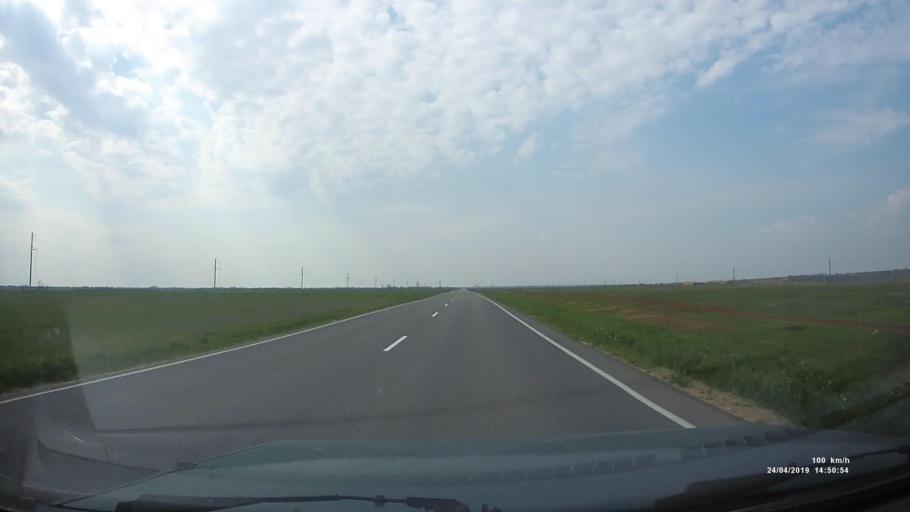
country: RU
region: Rostov
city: Remontnoye
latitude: 46.5207
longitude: 43.7111
